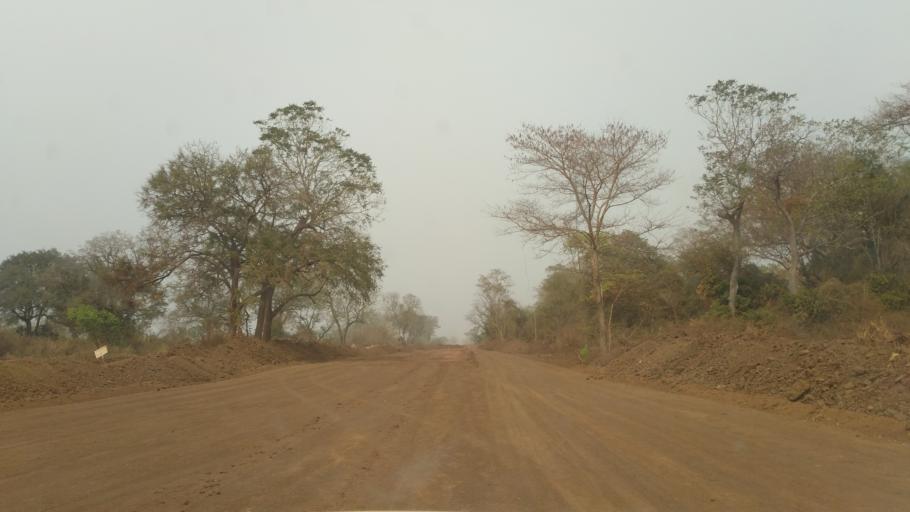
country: ET
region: Gambela
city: Gambela
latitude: 7.8624
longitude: 34.4787
